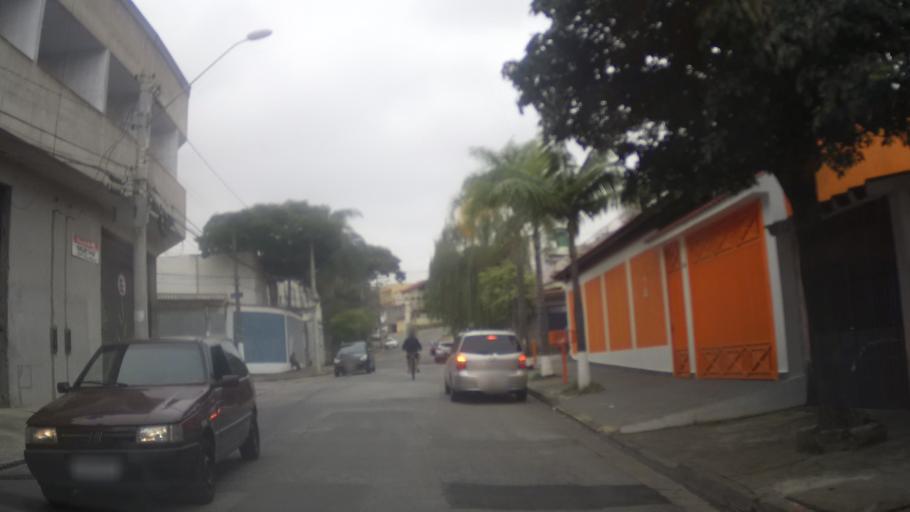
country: BR
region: Sao Paulo
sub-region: Guarulhos
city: Guarulhos
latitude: -23.4267
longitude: -46.5108
